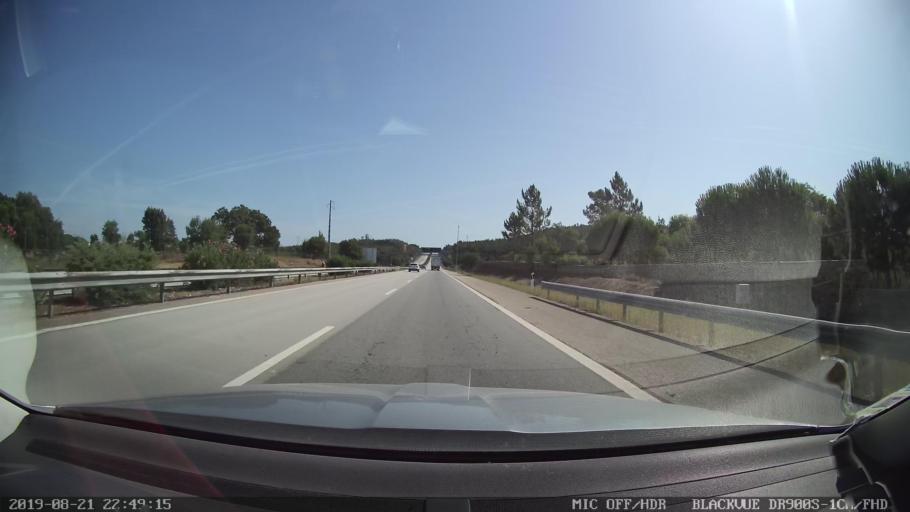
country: PT
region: Santarem
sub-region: Abrantes
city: Abrantes
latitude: 39.4857
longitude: -8.2184
